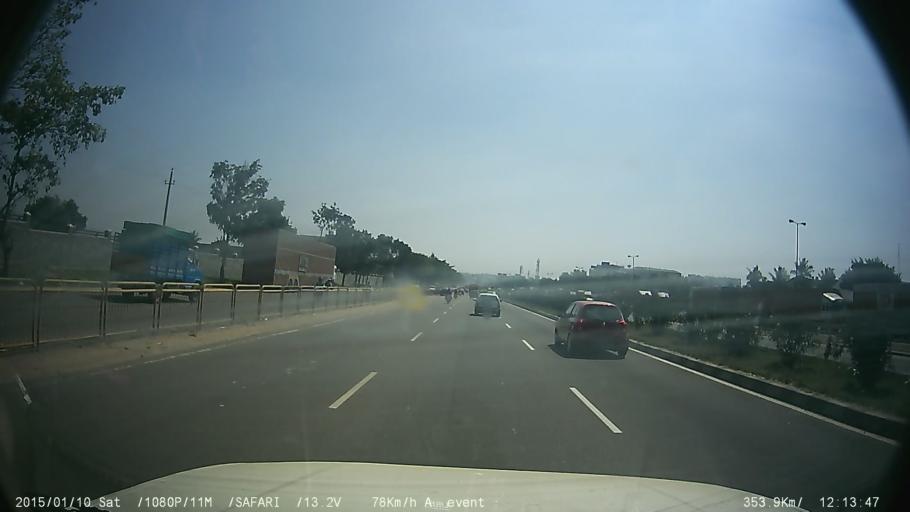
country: IN
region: Karnataka
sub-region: Bangalore Urban
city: Anekal
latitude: 12.8141
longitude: 77.6931
